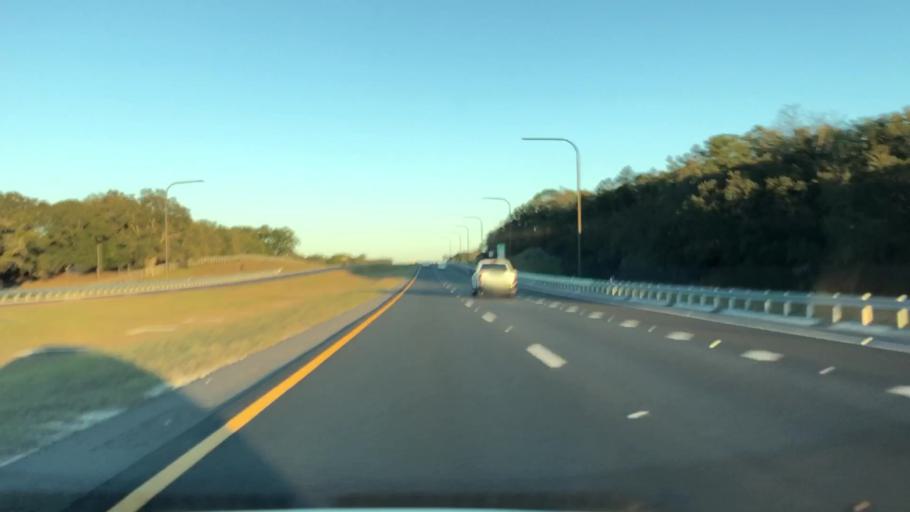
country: US
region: Florida
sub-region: Lake County
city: Mount Plymouth
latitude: 28.7756
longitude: -81.5503
